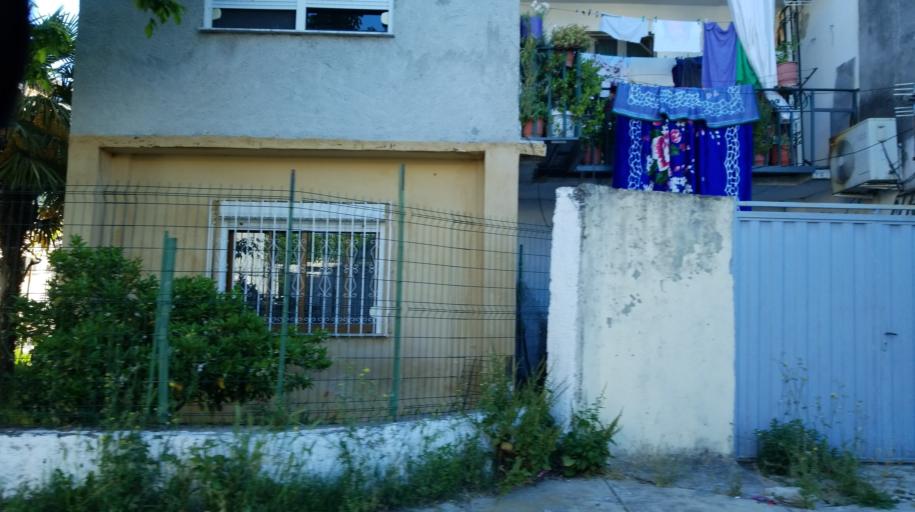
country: AL
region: Shkoder
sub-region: Rrethi i Shkodres
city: Shkoder
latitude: 42.0578
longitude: 19.5115
